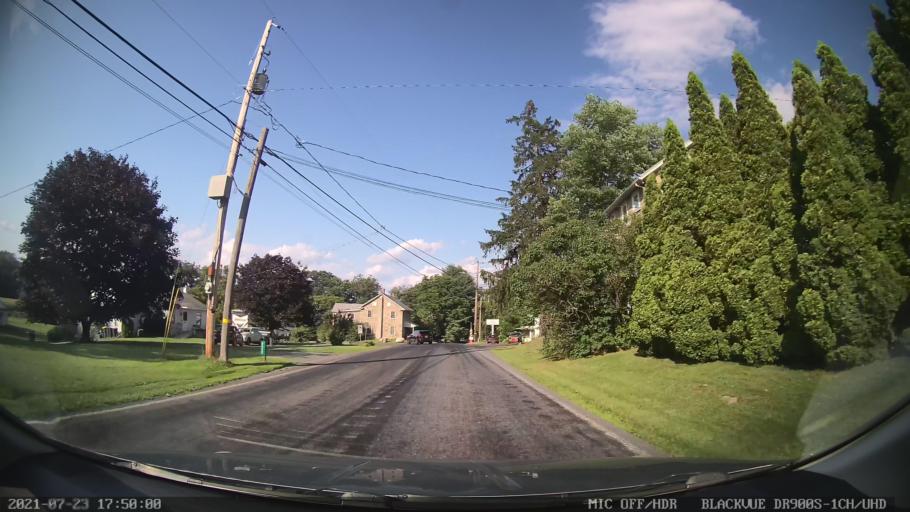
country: US
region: Pennsylvania
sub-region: Lehigh County
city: Alburtis
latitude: 40.4944
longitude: -75.6011
